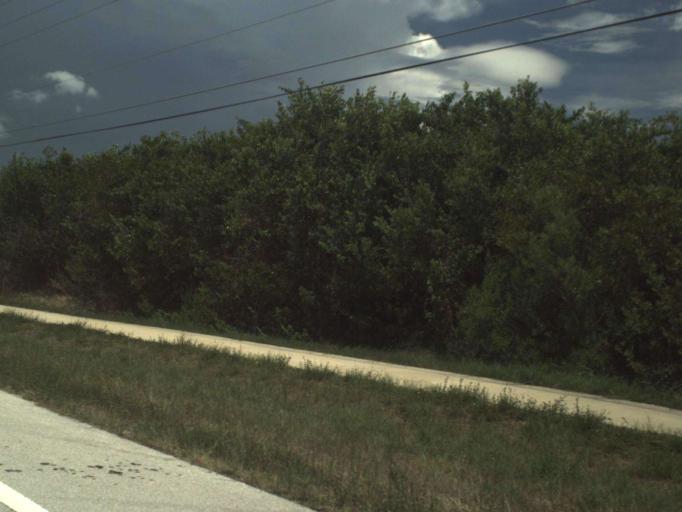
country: US
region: Florida
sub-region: Saint Lucie County
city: Fort Pierce
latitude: 27.4273
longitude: -80.2790
